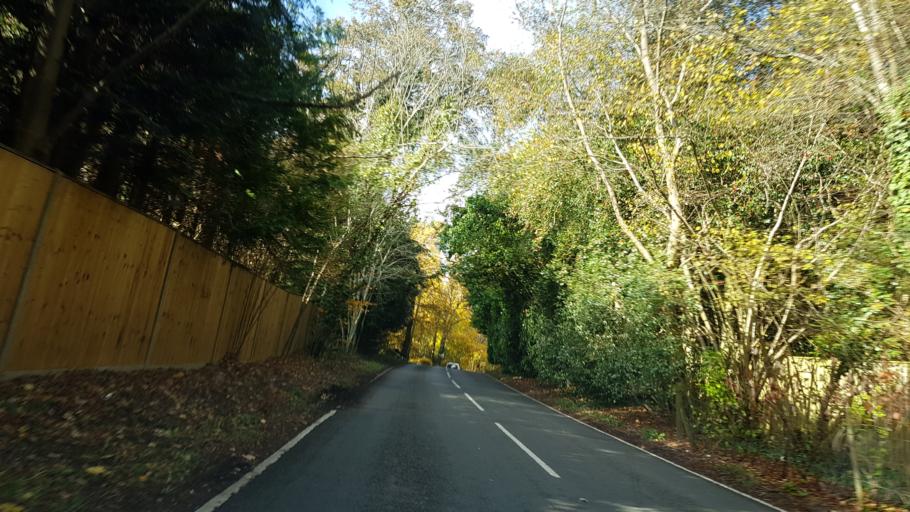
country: GB
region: England
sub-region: Surrey
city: Seale
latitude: 51.1949
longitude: -0.7408
